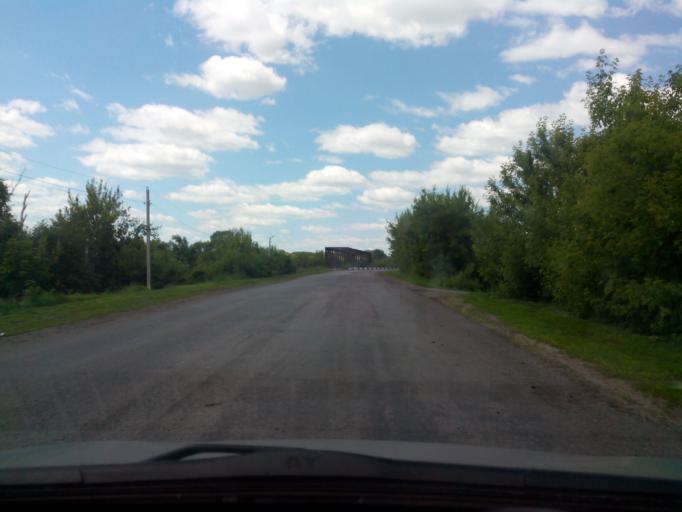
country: RU
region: Voronezj
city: Ternovka
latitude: 51.6236
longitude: 41.7738
